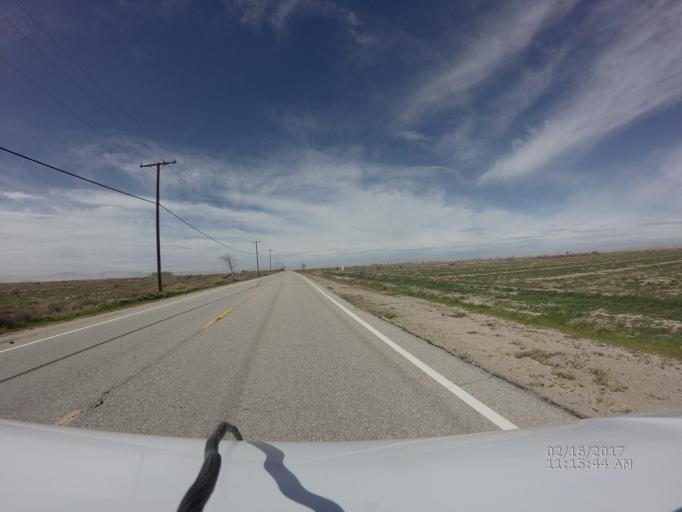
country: US
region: California
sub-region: Los Angeles County
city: Lake Los Angeles
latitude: 34.7196
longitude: -117.9600
